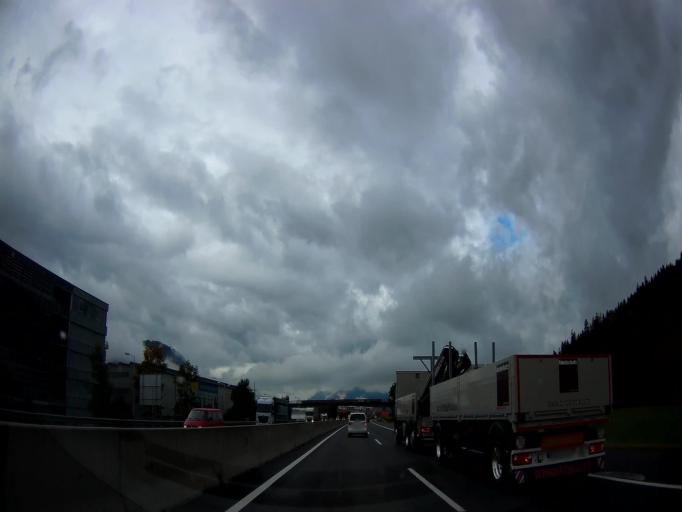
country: AT
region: Tyrol
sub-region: Politischer Bezirk Kufstein
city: Worgl
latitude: 47.4858
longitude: 12.0386
